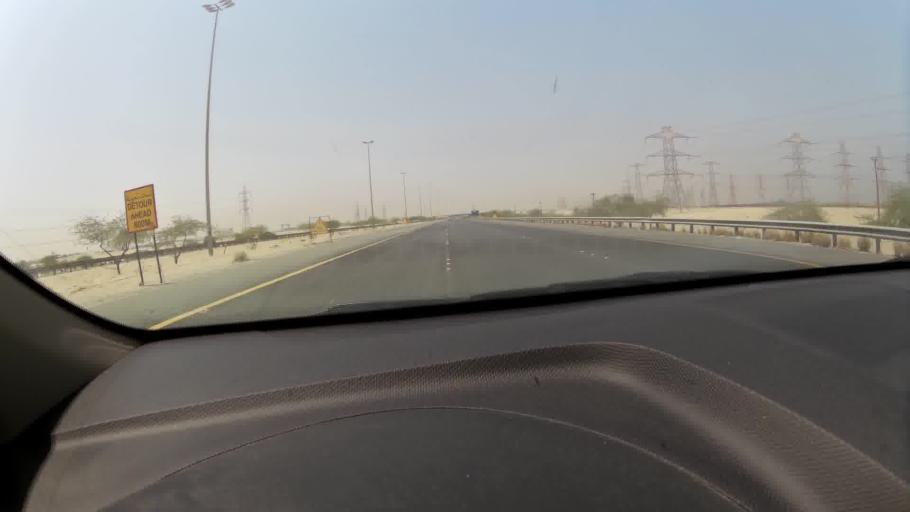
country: KW
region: Al Ahmadi
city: Al Fahahil
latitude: 28.9523
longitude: 48.1301
